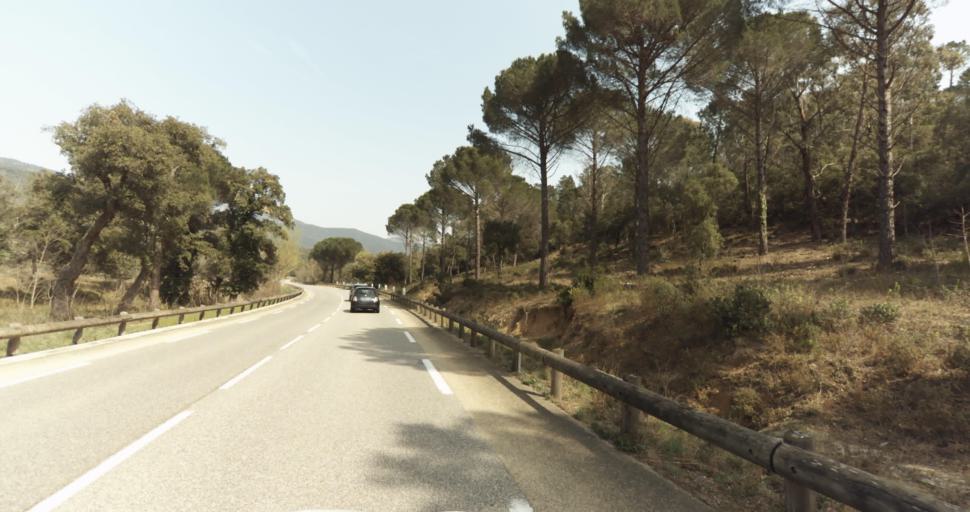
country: FR
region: Provence-Alpes-Cote d'Azur
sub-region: Departement du Var
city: Le Lavandou
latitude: 43.1925
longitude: 6.3770
